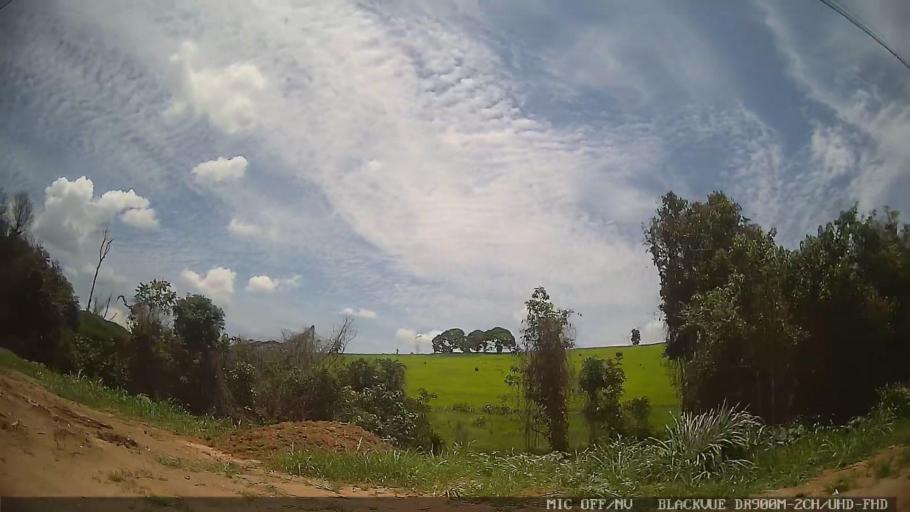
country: BR
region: Sao Paulo
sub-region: Atibaia
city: Atibaia
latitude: -23.0949
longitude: -46.6177
